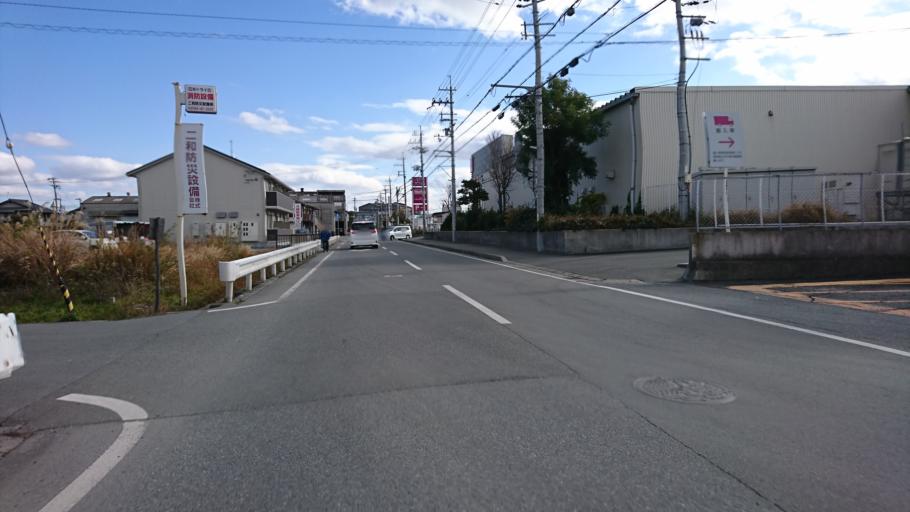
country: JP
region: Hyogo
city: Kakogawacho-honmachi
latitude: 34.7658
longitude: 134.7766
